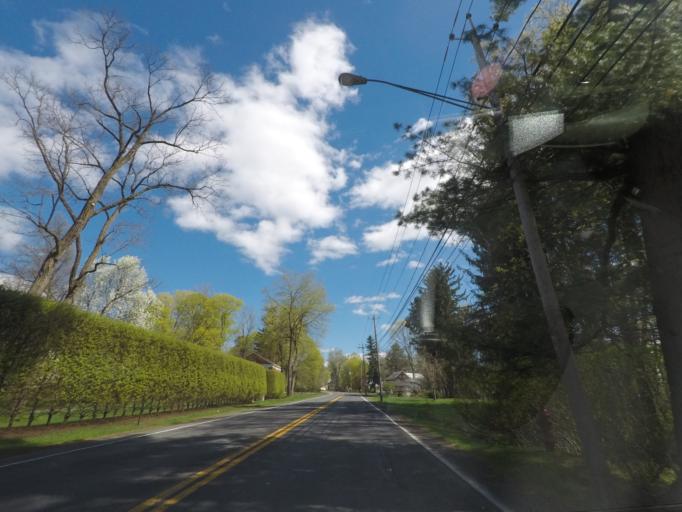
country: US
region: New York
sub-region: Columbia County
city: Oakdale
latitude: 42.2248
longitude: -73.7457
